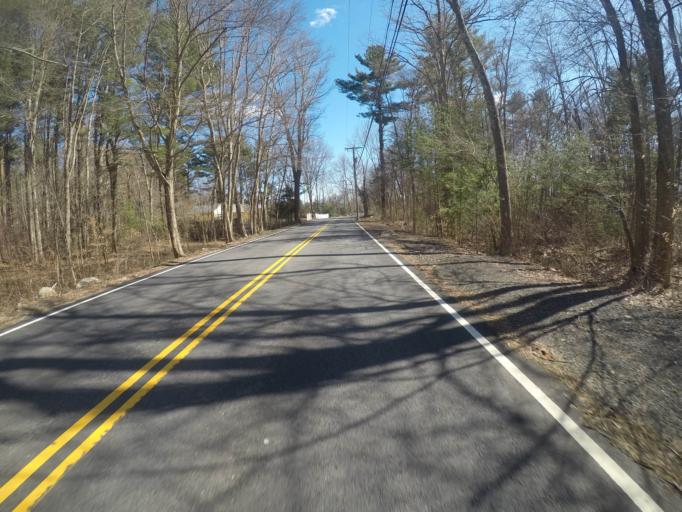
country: US
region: Massachusetts
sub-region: Bristol County
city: Easton
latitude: 42.0420
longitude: -71.1405
